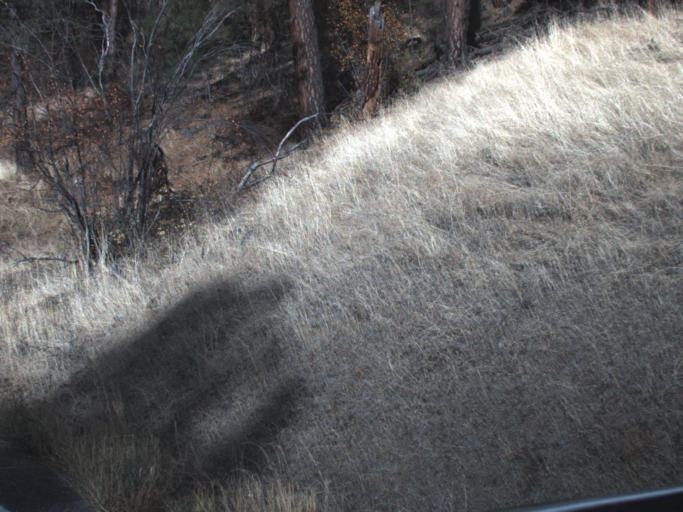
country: US
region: Washington
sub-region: Stevens County
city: Kettle Falls
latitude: 48.3303
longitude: -118.1544
